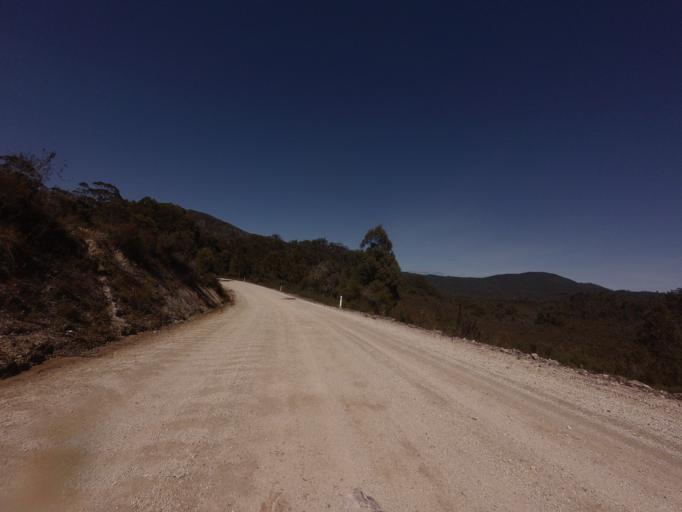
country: AU
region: Tasmania
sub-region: Huon Valley
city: Geeveston
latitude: -42.9114
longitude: 146.3619
